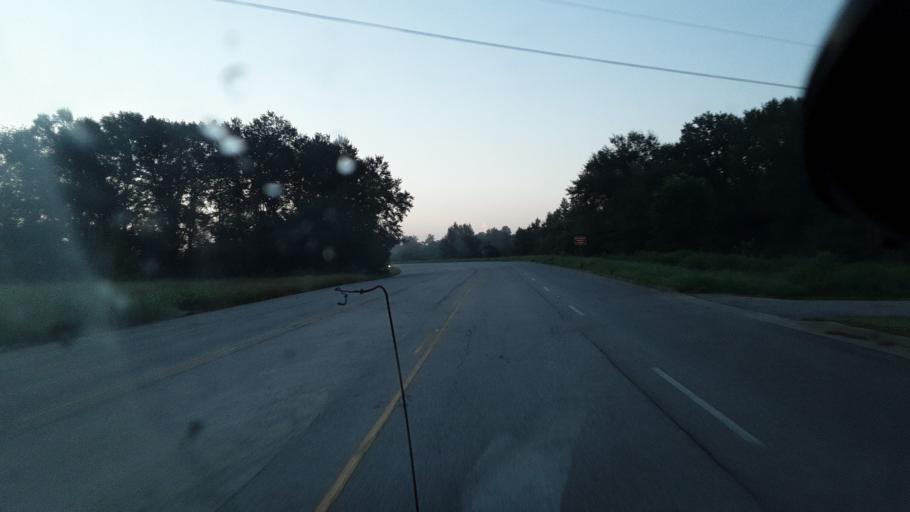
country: US
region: South Carolina
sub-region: Sumter County
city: South Sumter
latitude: 33.8793
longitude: -80.3417
